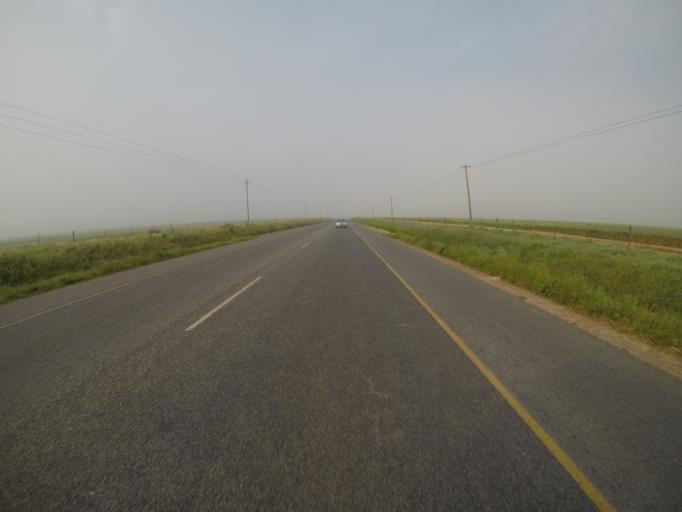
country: ZA
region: Western Cape
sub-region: West Coast District Municipality
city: Malmesbury
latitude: -33.6394
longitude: 18.7171
